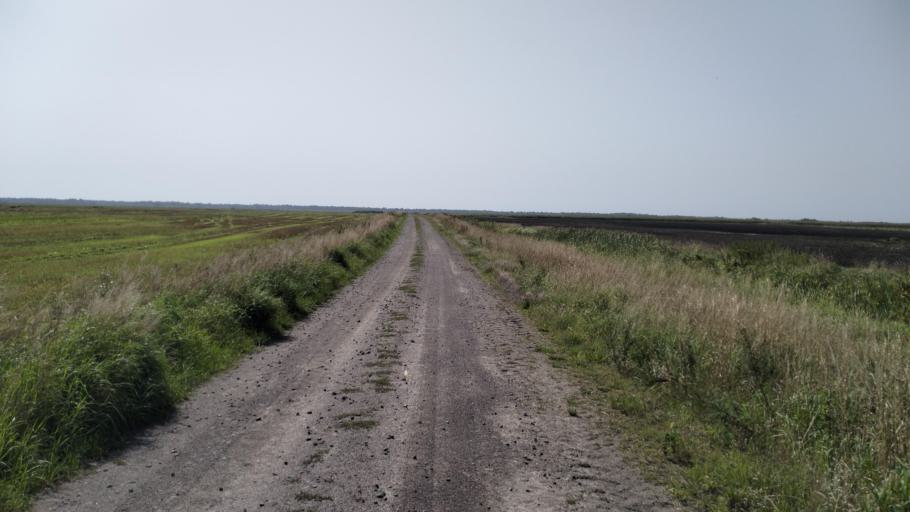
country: BY
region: Brest
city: Davyd-Haradok
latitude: 51.9963
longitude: 27.1650
